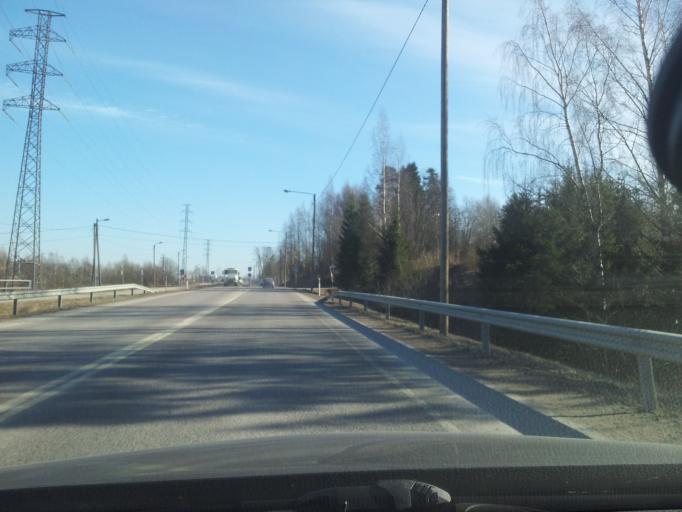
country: FI
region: Uusimaa
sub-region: Helsinki
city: Espoo
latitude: 60.1848
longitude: 24.5936
